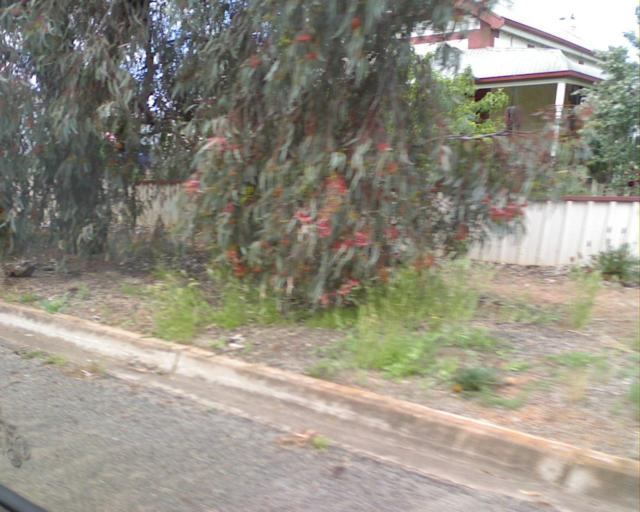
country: AU
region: South Australia
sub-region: Port Pirie City and Dists
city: Solomontown
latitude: -33.0345
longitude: 138.2714
